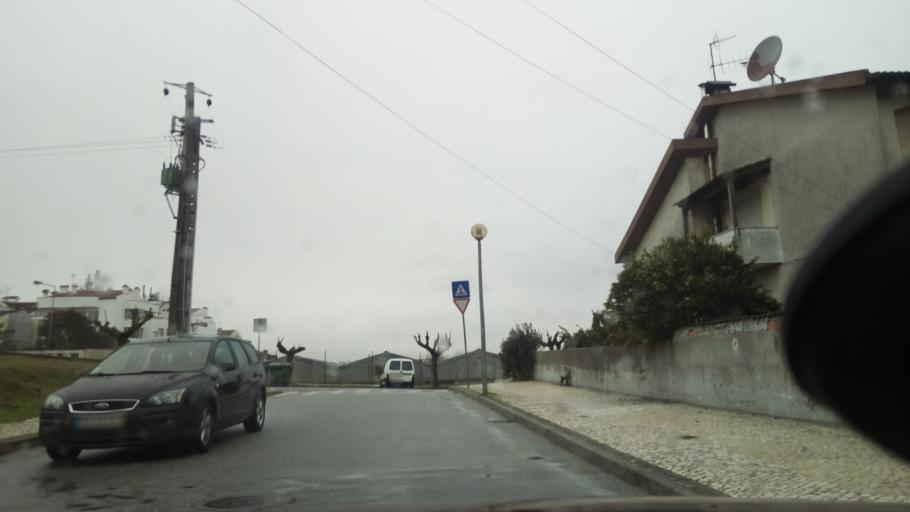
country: PT
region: Viseu
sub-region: Viseu
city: Rio de Loba
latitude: 40.6702
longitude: -7.8854
